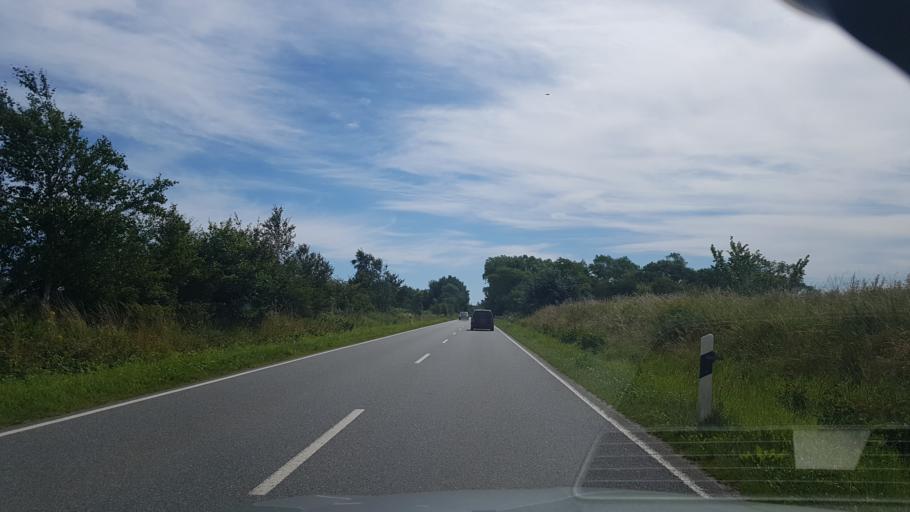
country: DE
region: Schleswig-Holstein
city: Wallsbull
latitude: 54.8011
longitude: 9.2662
